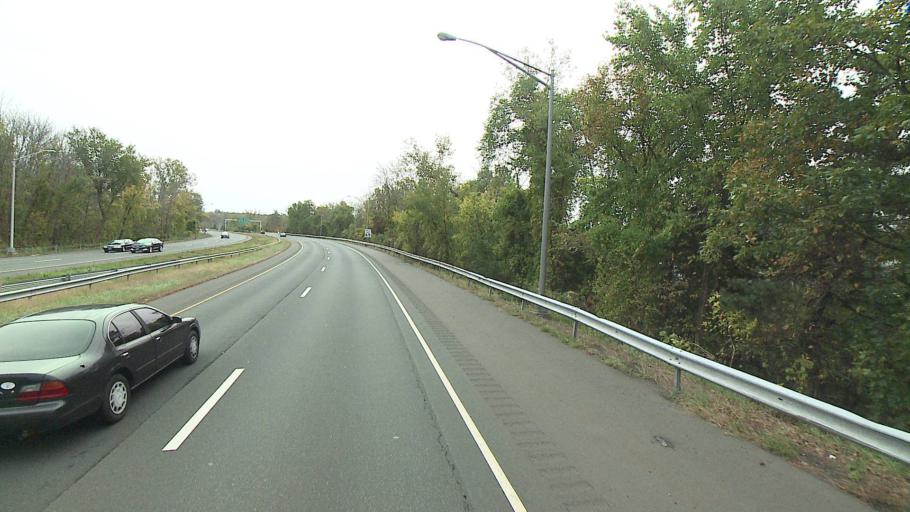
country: US
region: Connecticut
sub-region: Hartford County
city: Kensington
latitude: 41.6288
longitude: -72.7502
